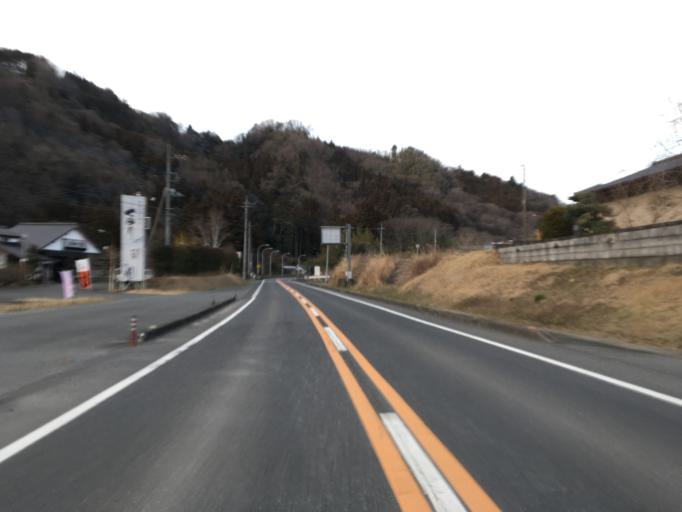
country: JP
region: Ibaraki
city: Daigo
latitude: 36.8300
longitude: 140.3789
